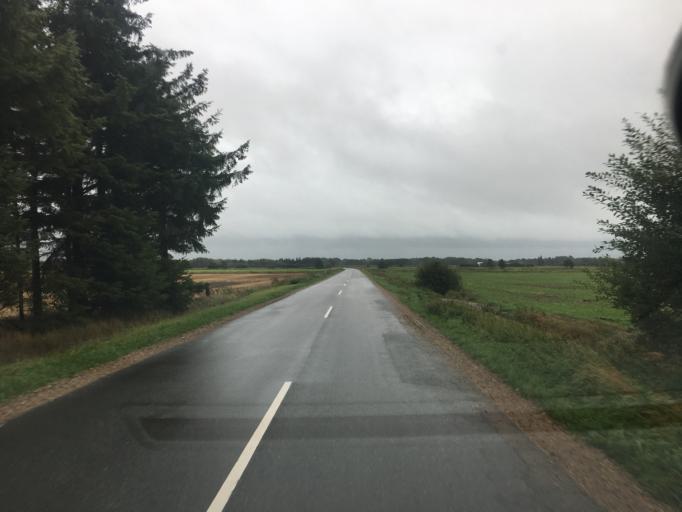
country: DE
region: Schleswig-Holstein
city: Bramstedtlund
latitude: 54.9713
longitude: 9.0443
